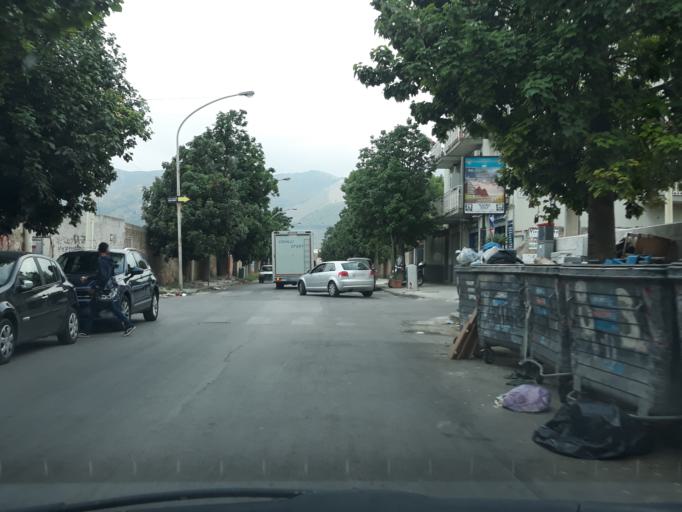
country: IT
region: Sicily
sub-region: Palermo
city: Monreale
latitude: 38.0941
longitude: 13.3196
